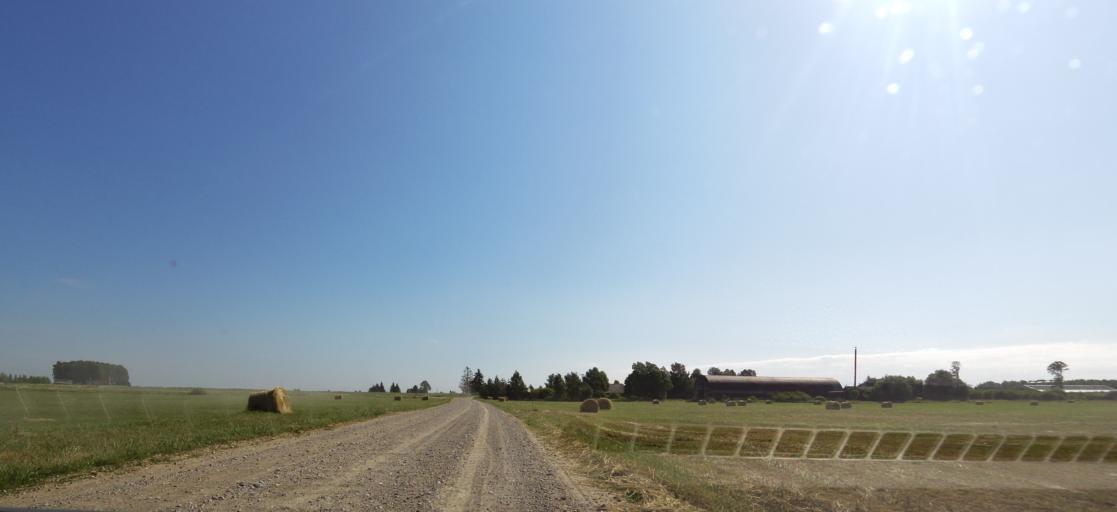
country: LT
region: Panevezys
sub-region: Birzai
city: Birzai
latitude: 56.2456
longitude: 24.8703
